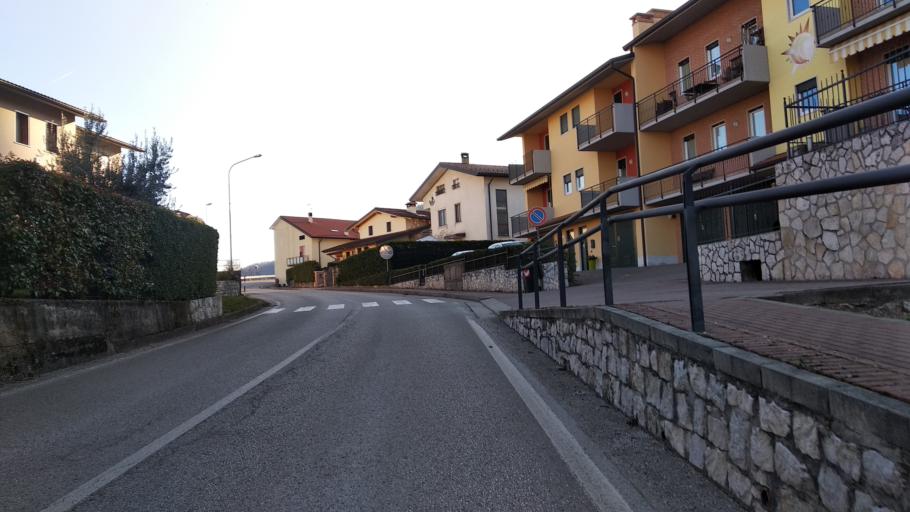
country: IT
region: Veneto
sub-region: Provincia di Vicenza
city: Monte di Malo
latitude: 45.6618
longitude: 11.3634
